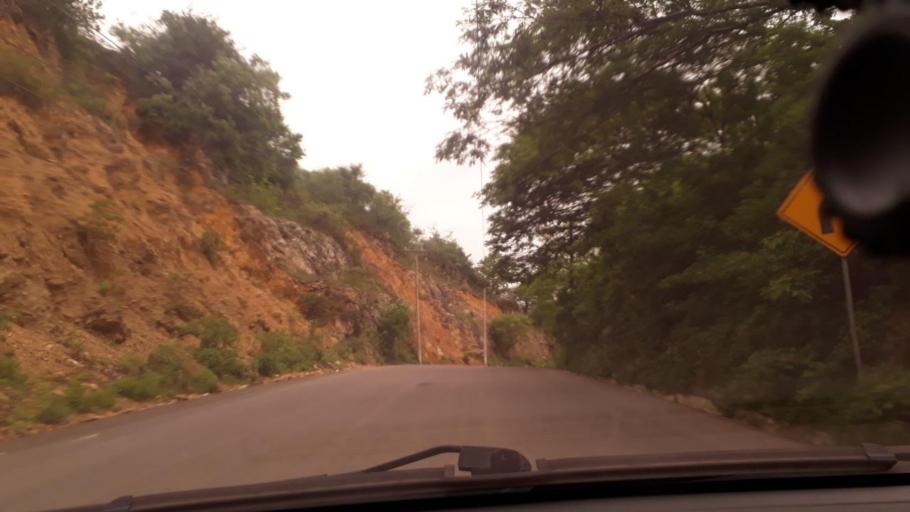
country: GT
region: Chiquimula
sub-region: Municipio de San Juan Ermita
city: San Juan Ermita
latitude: 14.7464
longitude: -89.4591
